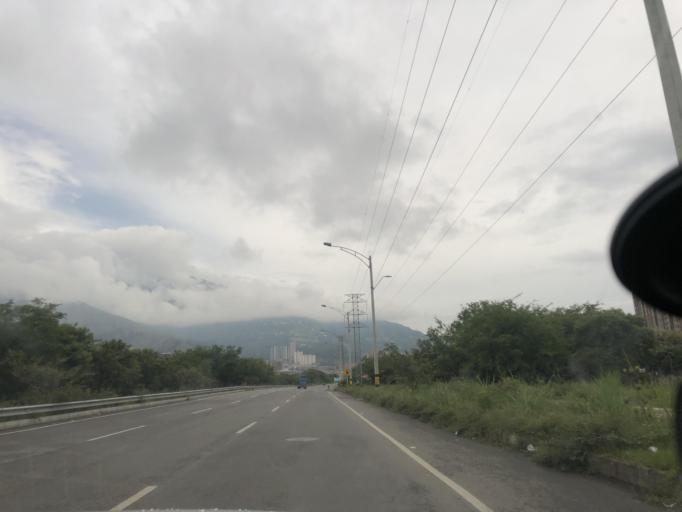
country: CO
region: Antioquia
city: Bello
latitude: 6.3248
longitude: -75.5528
